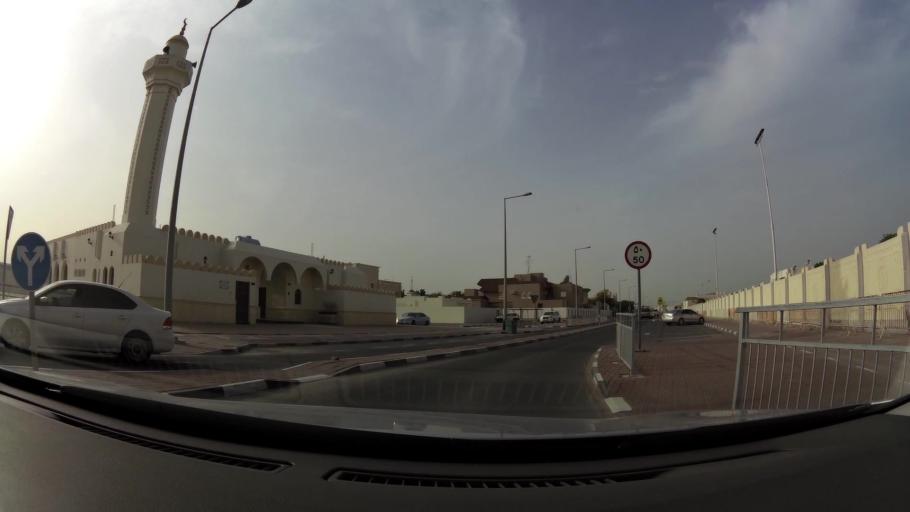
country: QA
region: Baladiyat ad Dawhah
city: Doha
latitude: 25.3258
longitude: 51.5204
